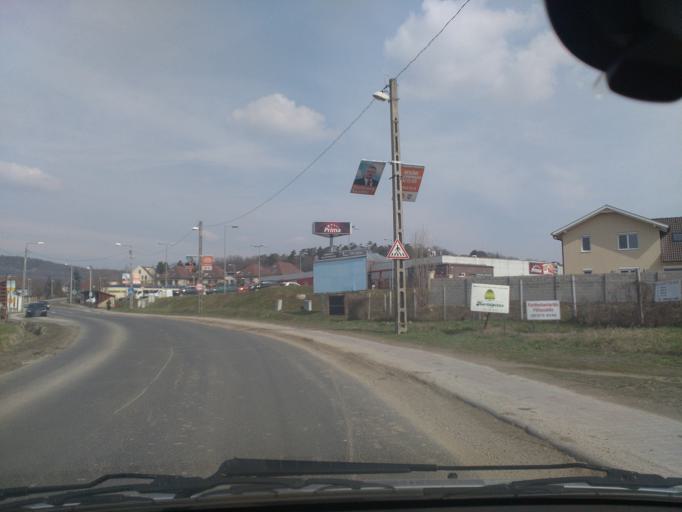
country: HU
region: Pest
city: Urom
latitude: 47.5894
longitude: 19.0099
